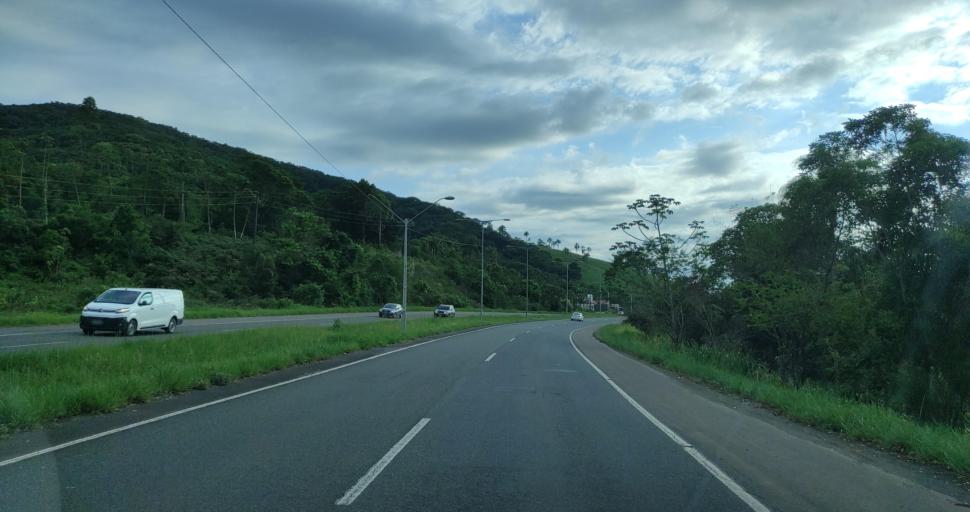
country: BR
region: Santa Catarina
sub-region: Penha
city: Penha
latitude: -26.8101
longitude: -48.6567
